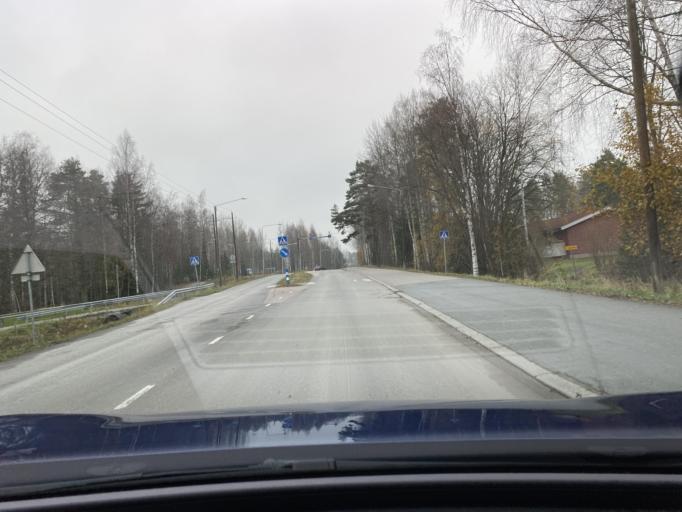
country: FI
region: Pirkanmaa
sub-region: Tampere
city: Nokia
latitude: 61.4607
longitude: 23.5038
